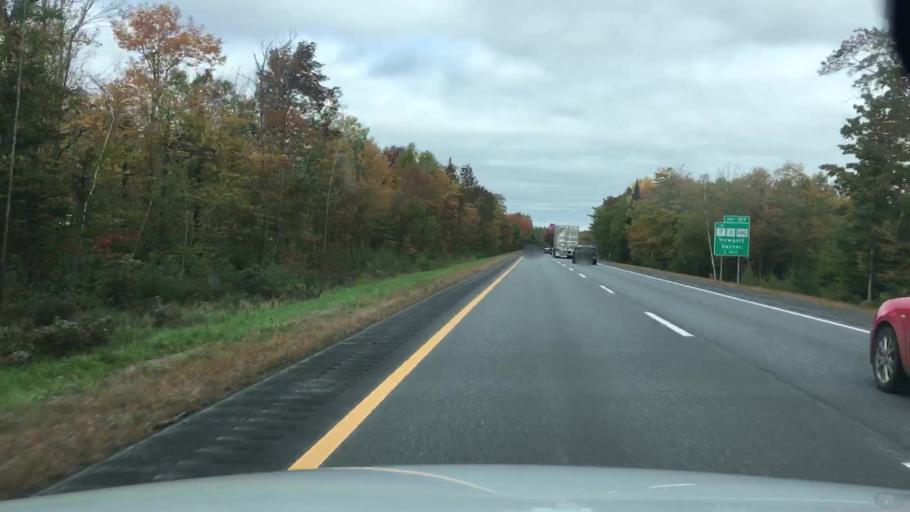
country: US
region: Maine
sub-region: Penobscot County
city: Newport
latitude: 44.8303
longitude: -69.3175
